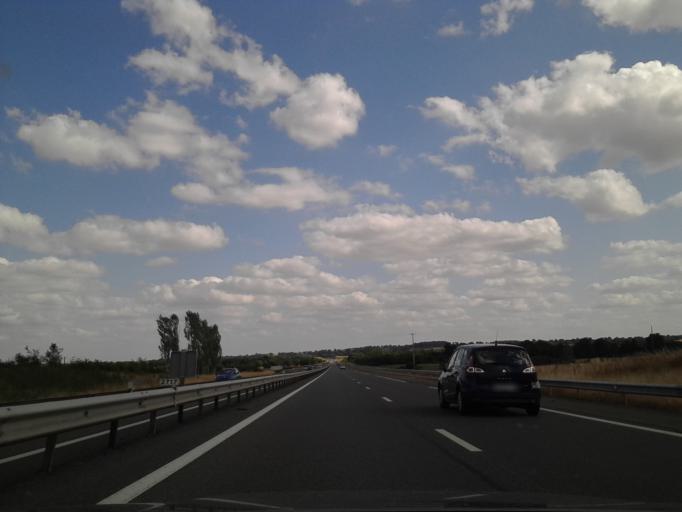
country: FR
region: Auvergne
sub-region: Departement de l'Allier
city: Vallon-en-Sully
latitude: 46.5524
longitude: 2.5489
